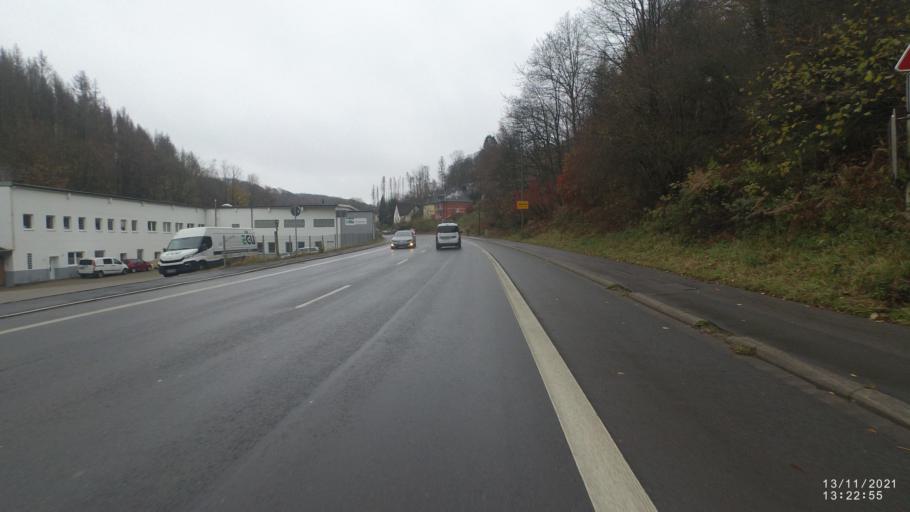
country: DE
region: North Rhine-Westphalia
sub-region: Regierungsbezirk Arnsberg
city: Luedenscheid
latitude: 51.2374
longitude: 7.6297
